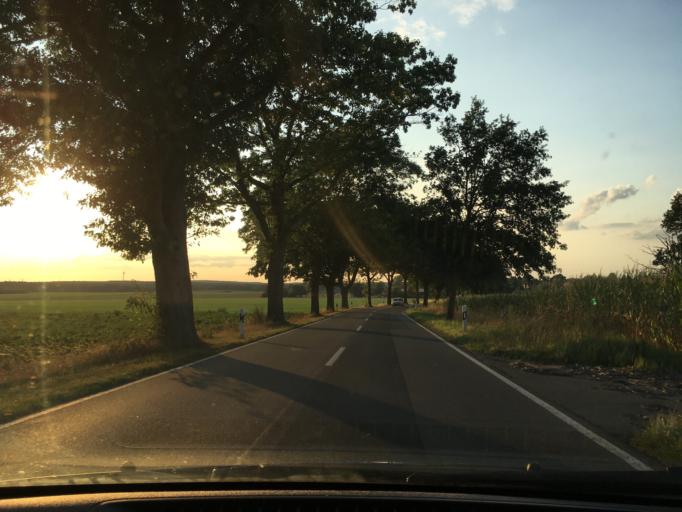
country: DE
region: Lower Saxony
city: Dahlem
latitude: 53.2485
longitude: 10.7729
